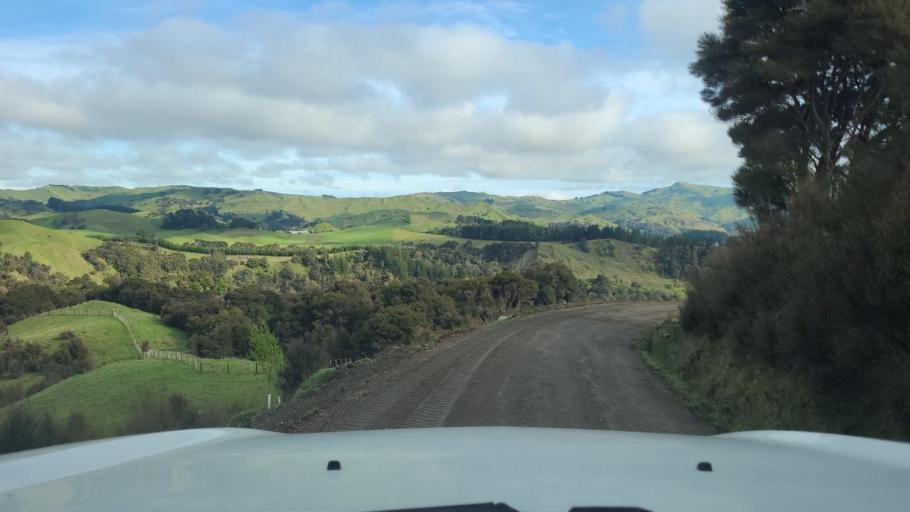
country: NZ
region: Wellington
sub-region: South Wairarapa District
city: Waipawa
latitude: -41.2403
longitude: 175.6947
